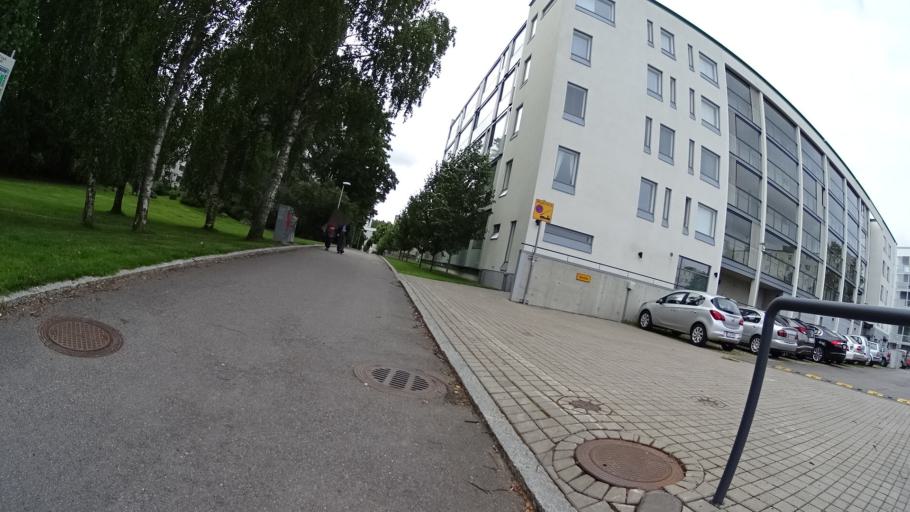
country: FI
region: Uusimaa
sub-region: Helsinki
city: Teekkarikylae
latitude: 60.2718
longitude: 24.8570
